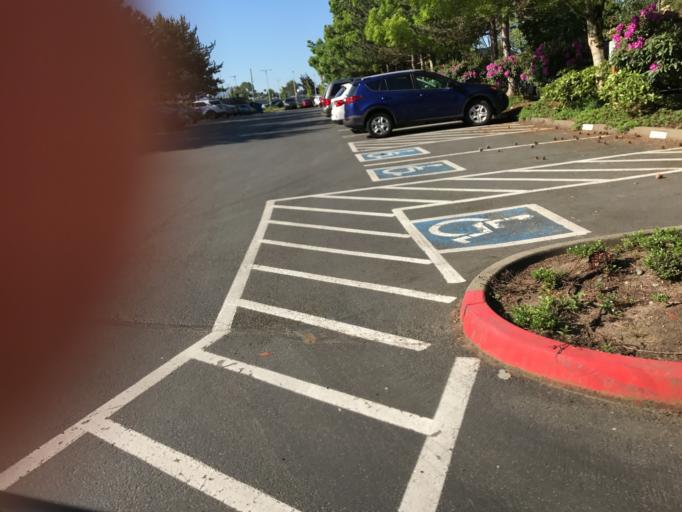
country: US
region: Washington
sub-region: King County
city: Bellevue
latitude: 47.6191
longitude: -122.1829
